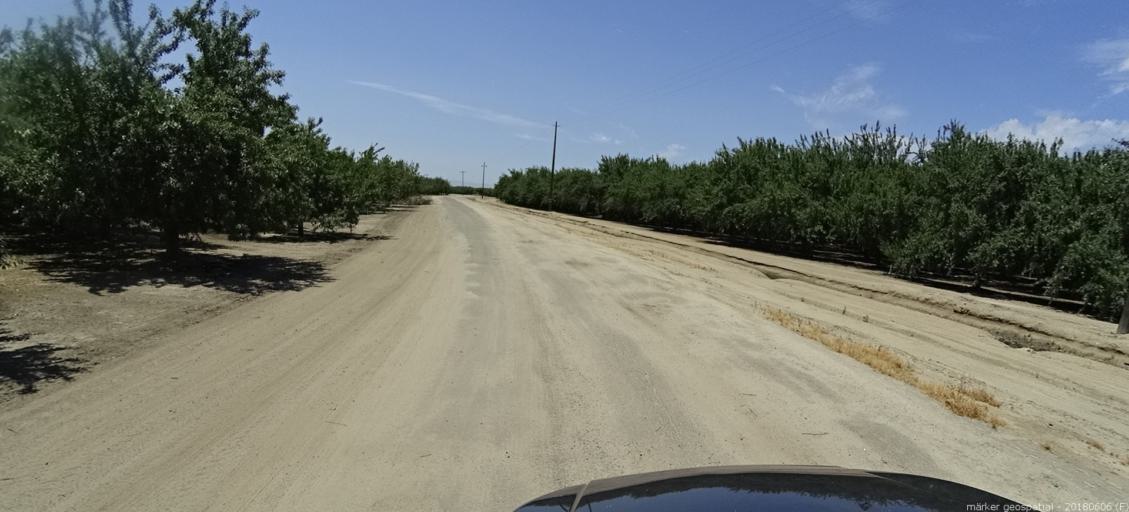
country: US
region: California
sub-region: Fresno County
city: Mendota
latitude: 36.8030
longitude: -120.3526
